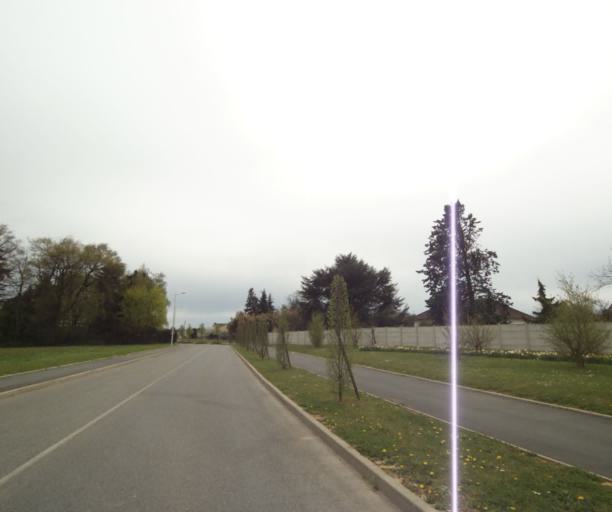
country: FR
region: Bourgogne
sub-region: Departement de Saone-et-Loire
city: Charnay-les-Macon
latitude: 46.3118
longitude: 4.8021
